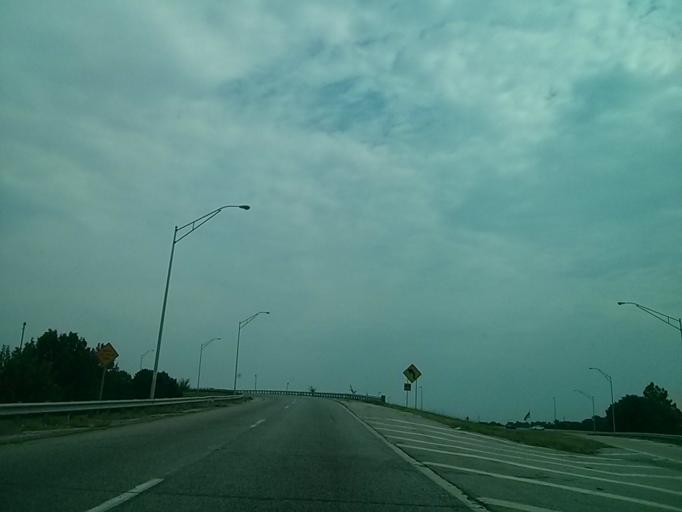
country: US
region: Oklahoma
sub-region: Tulsa County
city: Owasso
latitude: 36.1631
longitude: -95.8603
